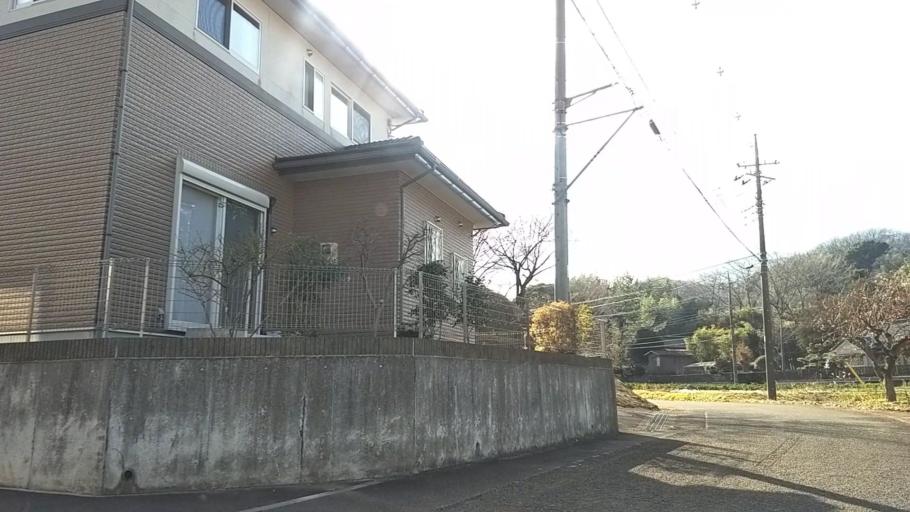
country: JP
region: Kanagawa
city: Isehara
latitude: 35.4285
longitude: 139.3170
